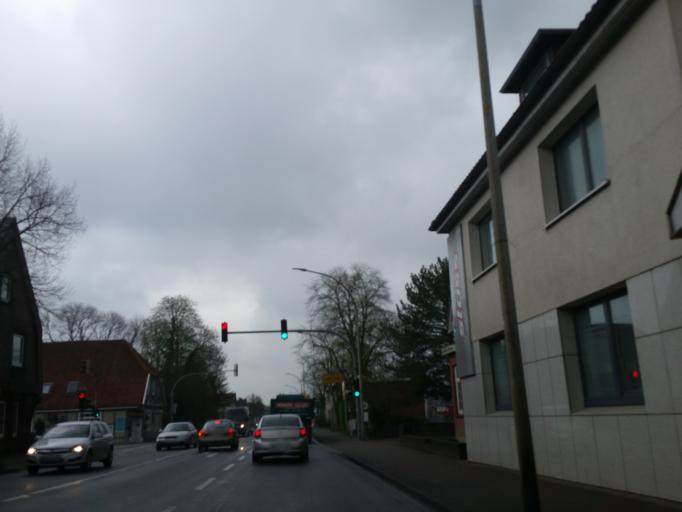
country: DE
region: Lower Saxony
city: Bremervorde
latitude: 53.4905
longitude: 9.1344
